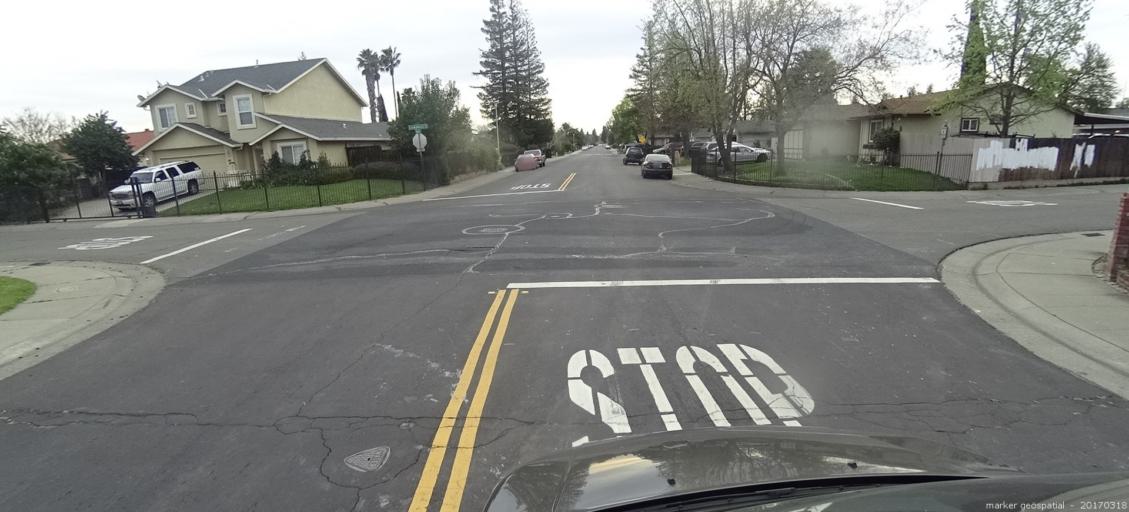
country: US
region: California
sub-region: Sacramento County
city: Parkway
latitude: 38.4874
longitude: -121.4648
